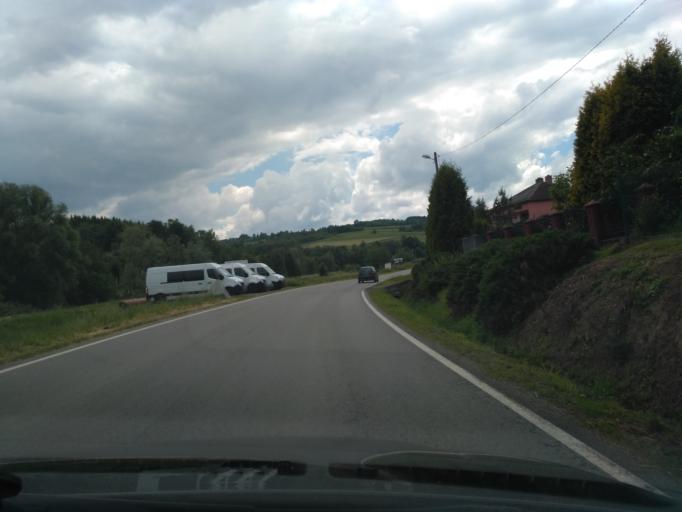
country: PL
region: Subcarpathian Voivodeship
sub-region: Powiat przeworski
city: Jawornik Polski
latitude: 49.9049
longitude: 22.3078
